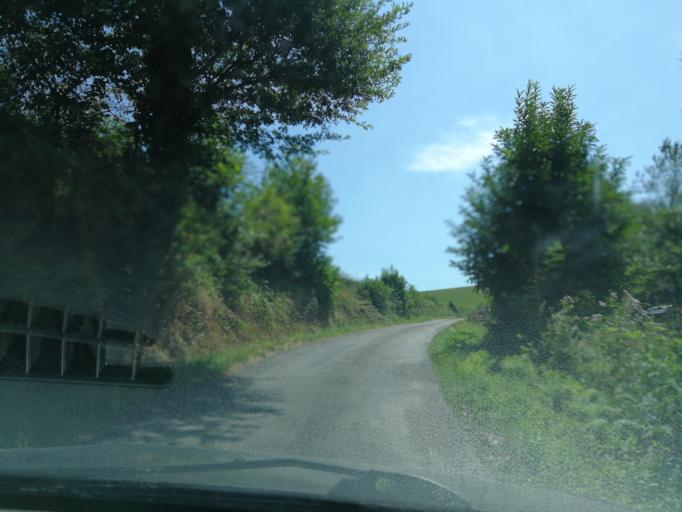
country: FR
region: Midi-Pyrenees
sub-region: Departement de l'Aveyron
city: Livinhac-le-Haut
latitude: 44.6731
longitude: 2.3264
